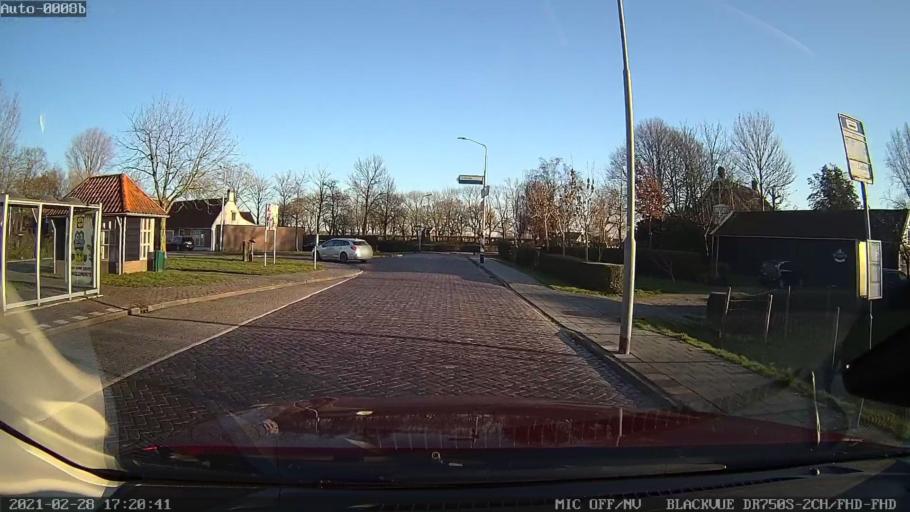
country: NL
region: Zeeland
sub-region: Schouwen-Duiveland
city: Bruinisse
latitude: 51.6882
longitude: 3.9806
